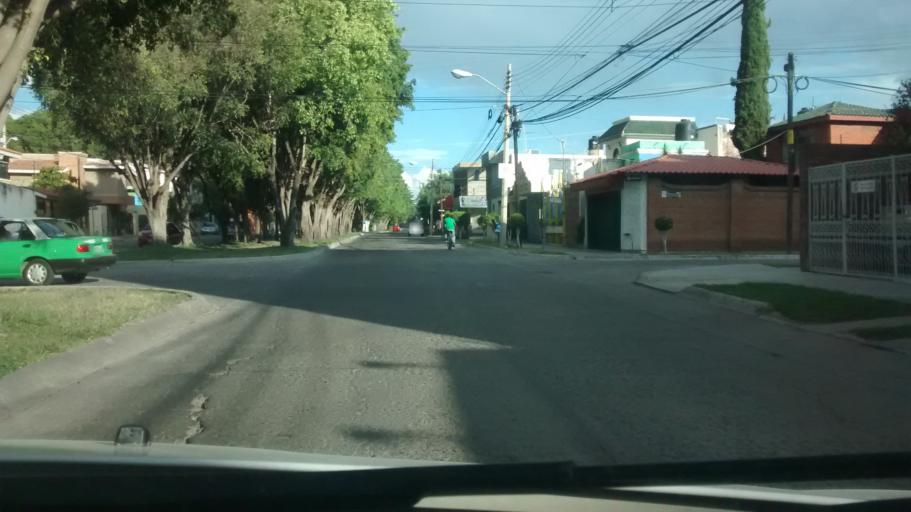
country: MX
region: Guanajuato
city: Leon
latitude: 21.1003
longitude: -101.6456
